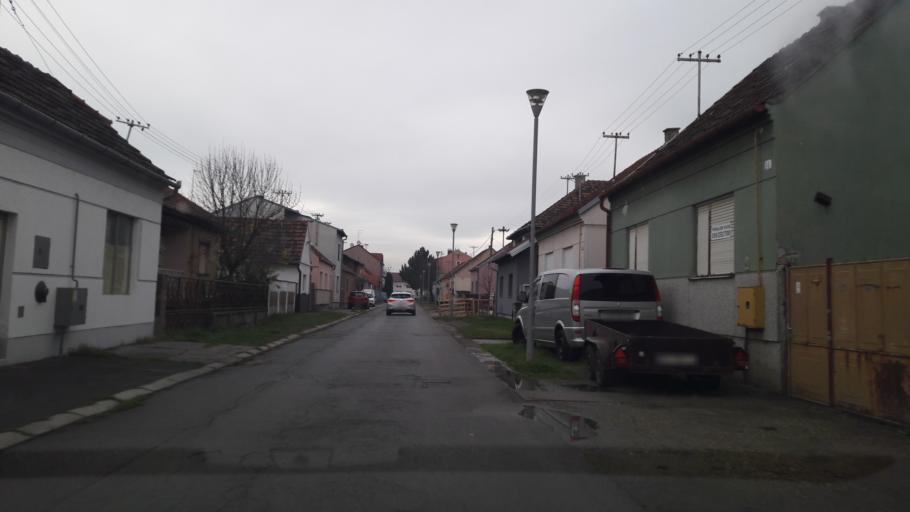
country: HR
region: Osjecko-Baranjska
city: Visnjevac
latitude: 45.5677
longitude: 18.6185
